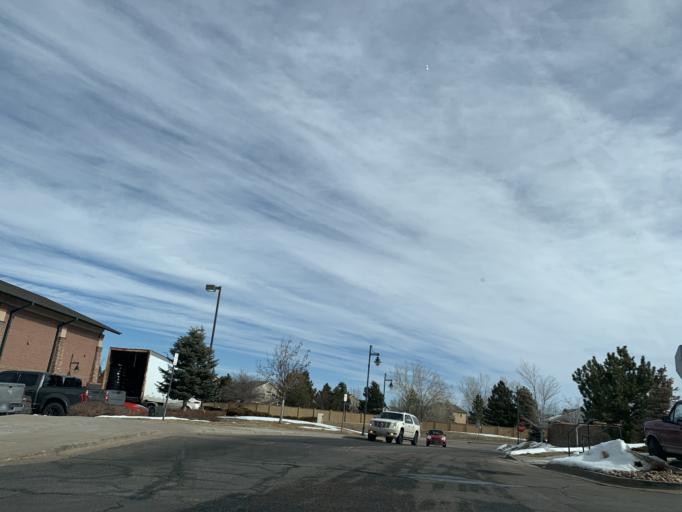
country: US
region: Colorado
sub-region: Douglas County
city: Highlands Ranch
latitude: 39.5262
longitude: -104.9407
